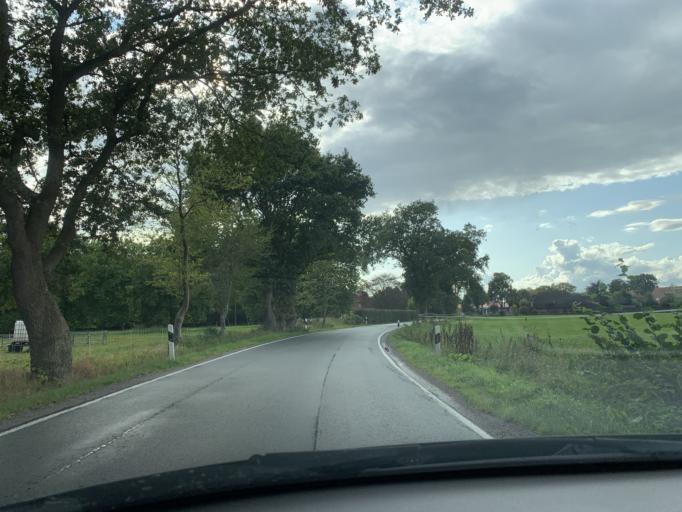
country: DE
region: Lower Saxony
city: Westerstede
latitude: 53.3165
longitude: 7.9272
